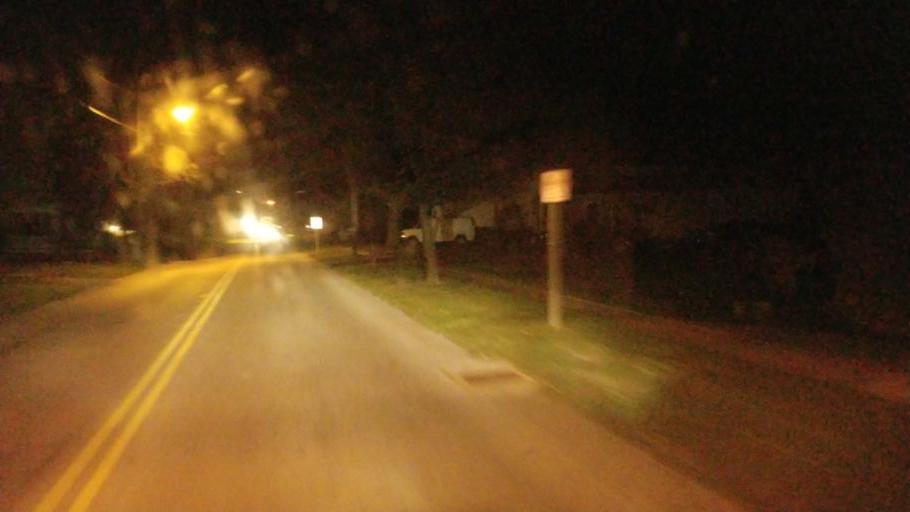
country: US
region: Ohio
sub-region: Hancock County
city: Arlington
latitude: 40.7922
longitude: -83.6442
